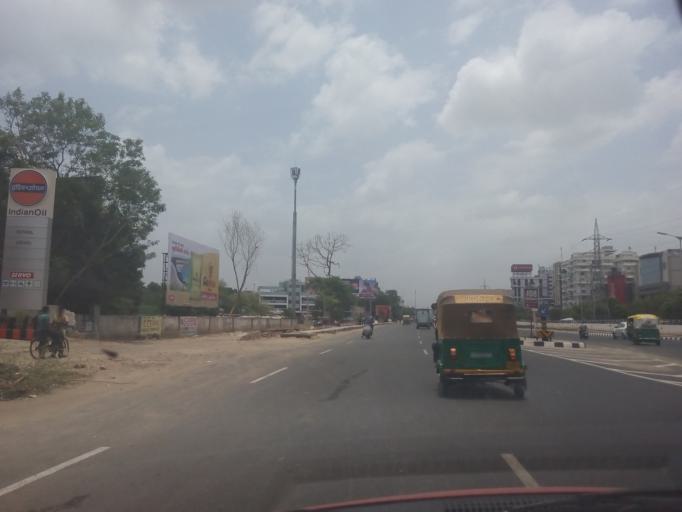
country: IN
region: Gujarat
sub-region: Ahmadabad
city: Sarkhej
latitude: 23.0411
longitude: 72.5129
